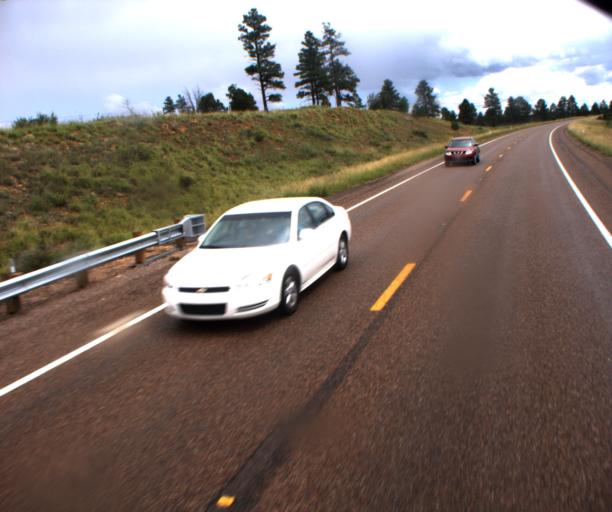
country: US
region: Arizona
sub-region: Navajo County
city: Linden
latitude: 34.3638
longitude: -110.3307
